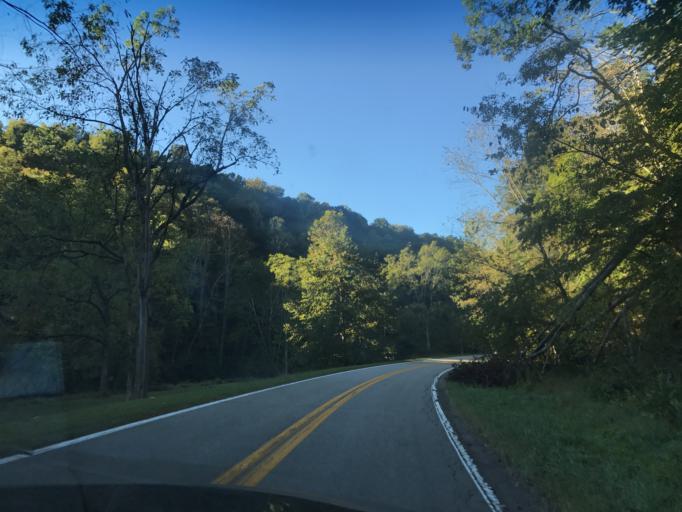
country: US
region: West Virginia
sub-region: Pleasants County
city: Saint Marys
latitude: 39.2605
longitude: -81.2072
